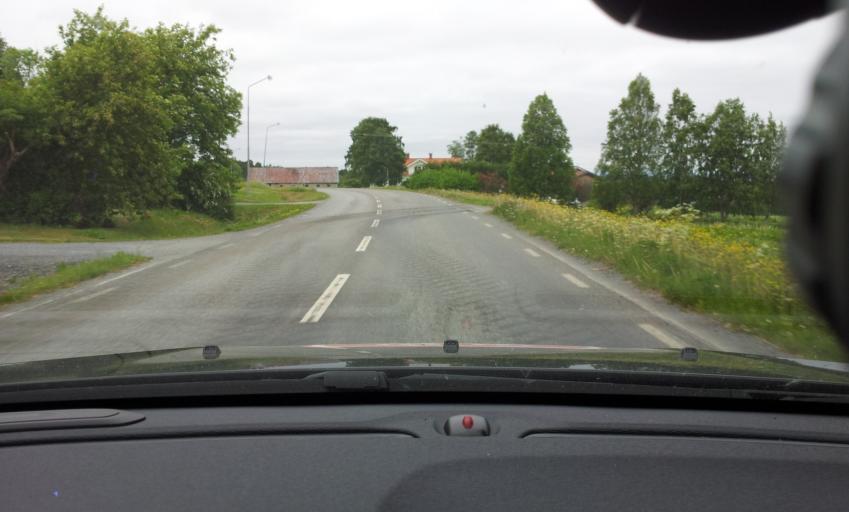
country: SE
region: Jaemtland
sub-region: Krokoms Kommun
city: Krokom
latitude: 63.1339
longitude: 14.2761
